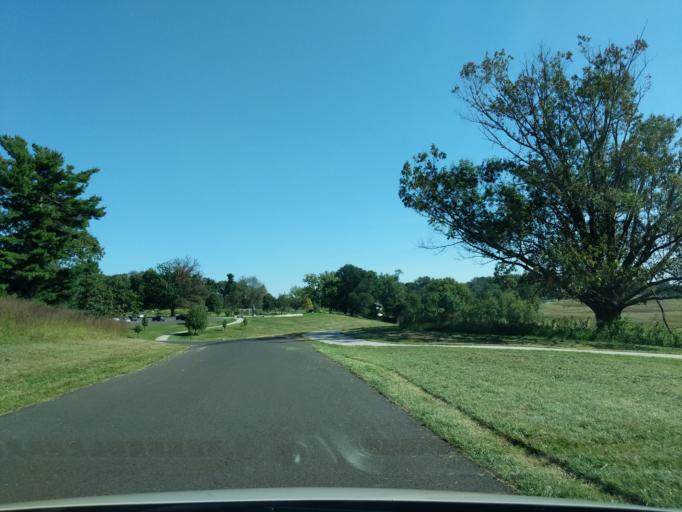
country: US
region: Pennsylvania
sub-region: Chester County
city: Chesterbrook
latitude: 40.1015
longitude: -75.4482
